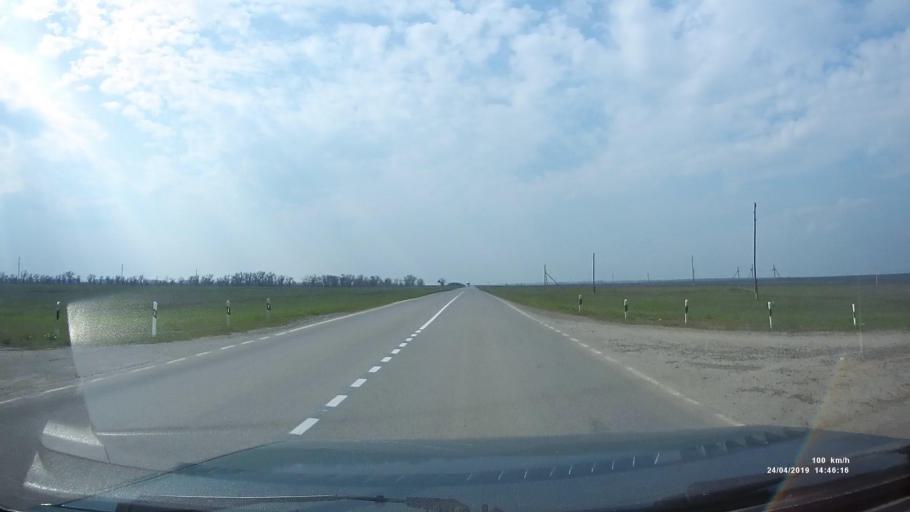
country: RU
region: Rostov
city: Remontnoye
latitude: 46.4803
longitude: 43.7929
